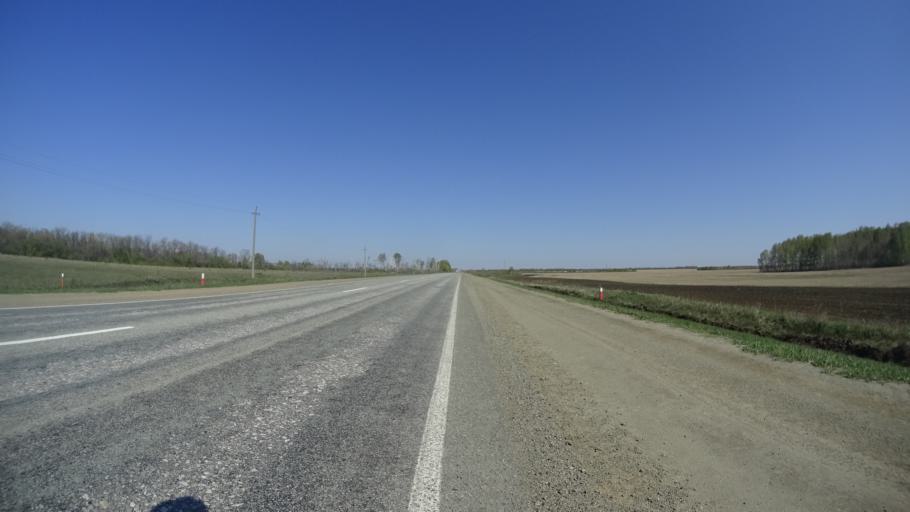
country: RU
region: Chelyabinsk
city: Troitsk
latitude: 54.1923
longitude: 61.4333
